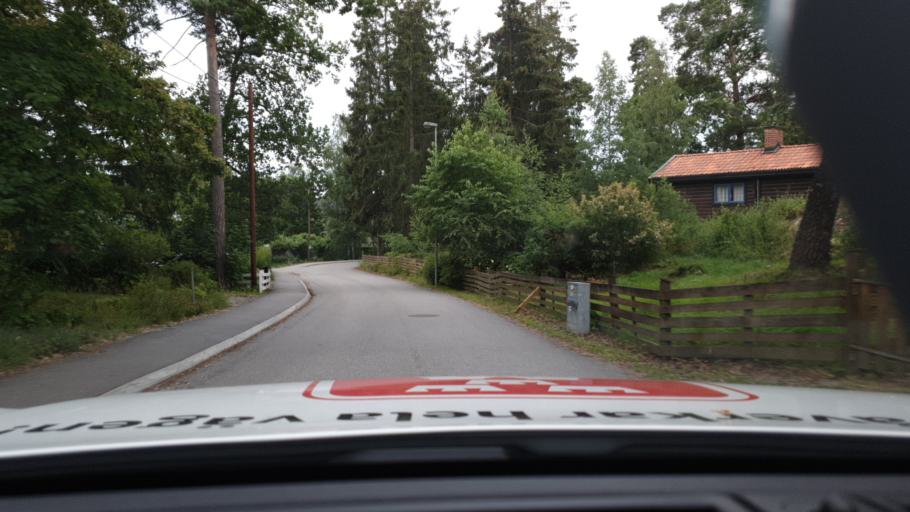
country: SE
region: Stockholm
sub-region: Osterakers Kommun
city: Akersberga
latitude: 59.4581
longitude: 18.3085
